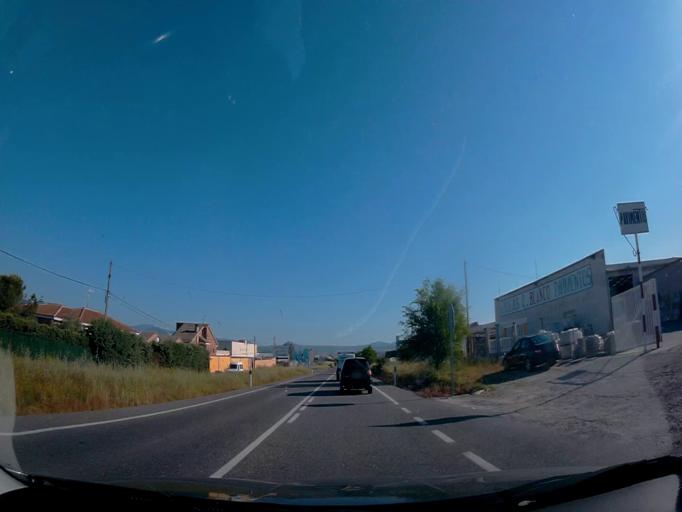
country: ES
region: Castille-La Mancha
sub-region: Province of Toledo
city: Escalona
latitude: 40.1314
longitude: -4.4049
